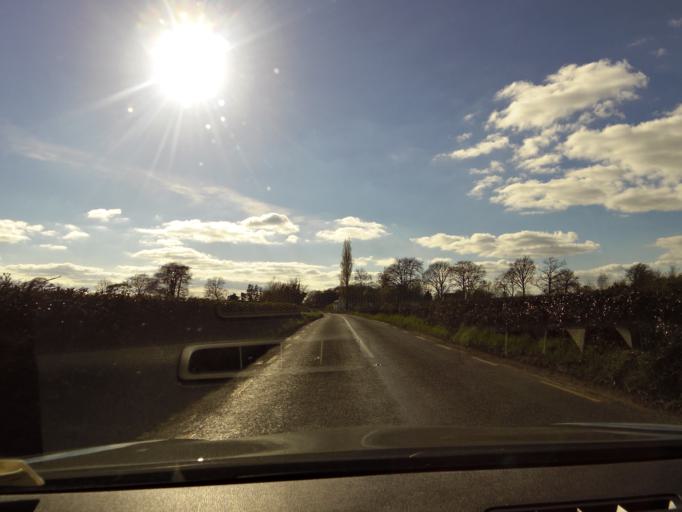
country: IE
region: Leinster
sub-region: Uibh Fhaili
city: Banagher
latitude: 53.1065
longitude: -8.0556
